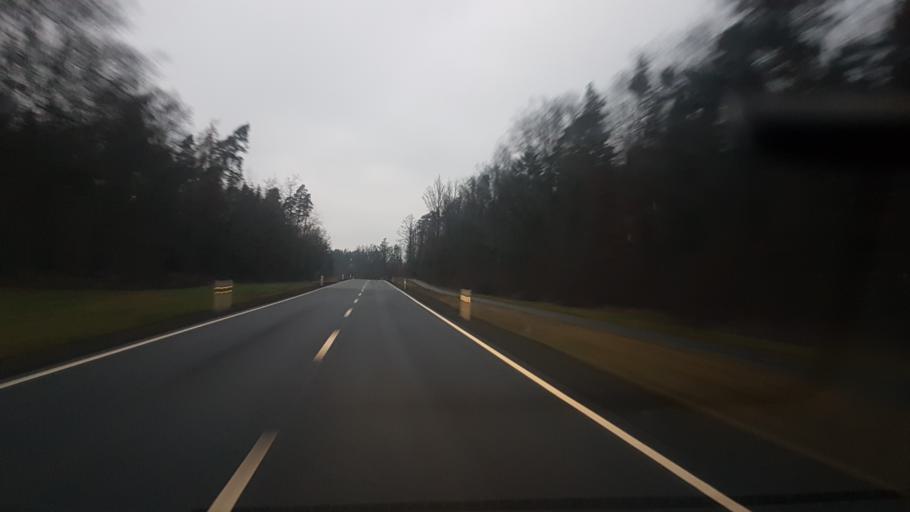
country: DE
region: Bavaria
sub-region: Regierungsbezirk Unterfranken
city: Ermershausen
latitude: 50.2208
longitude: 10.6002
